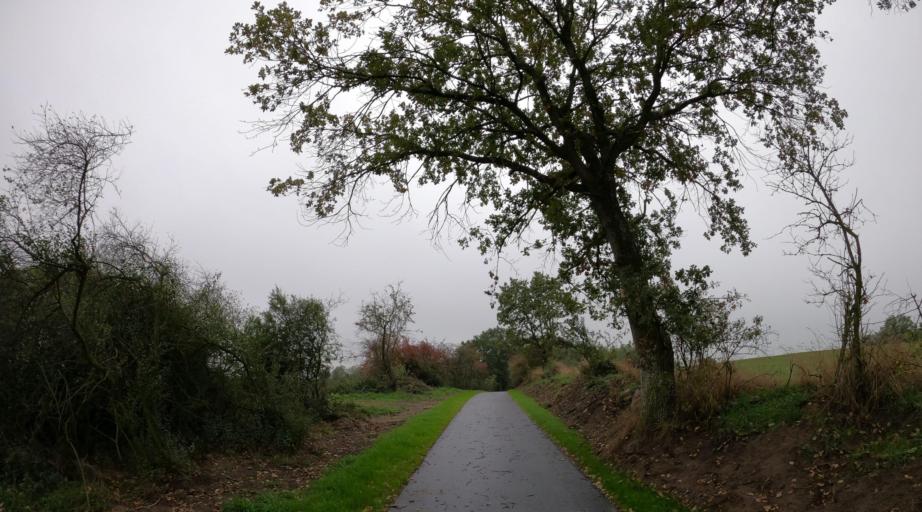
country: PL
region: West Pomeranian Voivodeship
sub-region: Powiat mysliborski
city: Mysliborz
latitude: 52.9118
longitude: 14.7466
